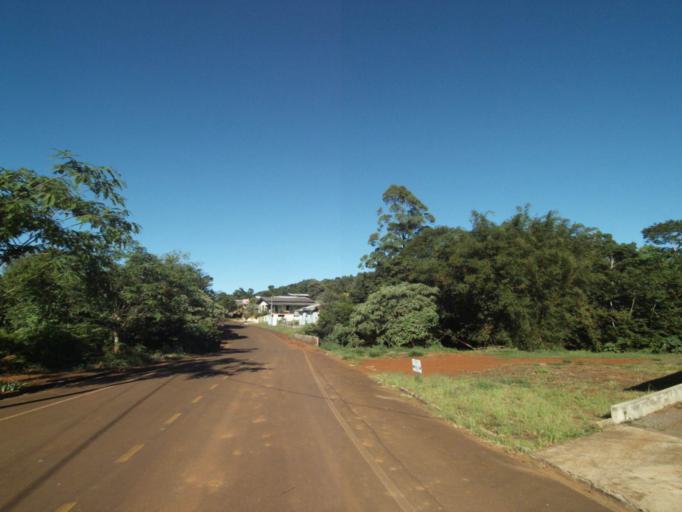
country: BR
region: Parana
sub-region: Pato Branco
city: Pato Branco
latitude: -26.2621
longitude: -52.7790
